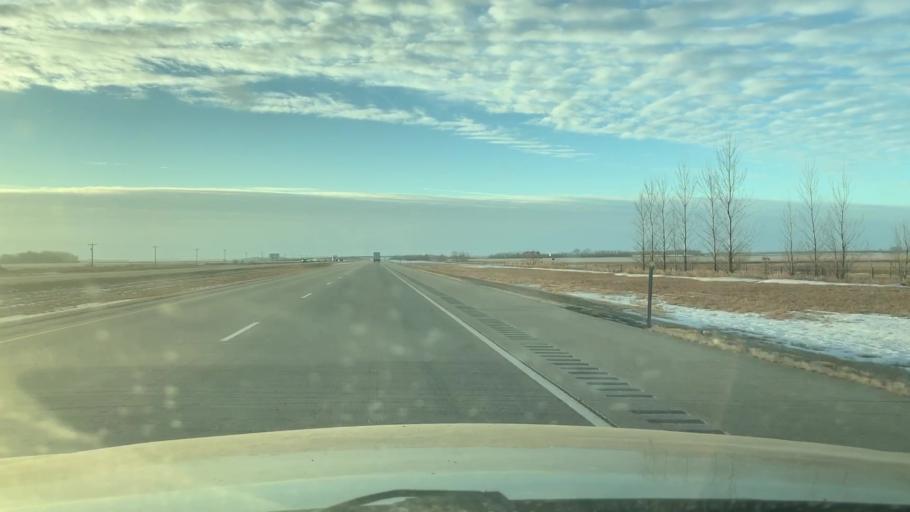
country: US
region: North Dakota
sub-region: Cass County
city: Casselton
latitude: 46.8759
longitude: -97.3220
